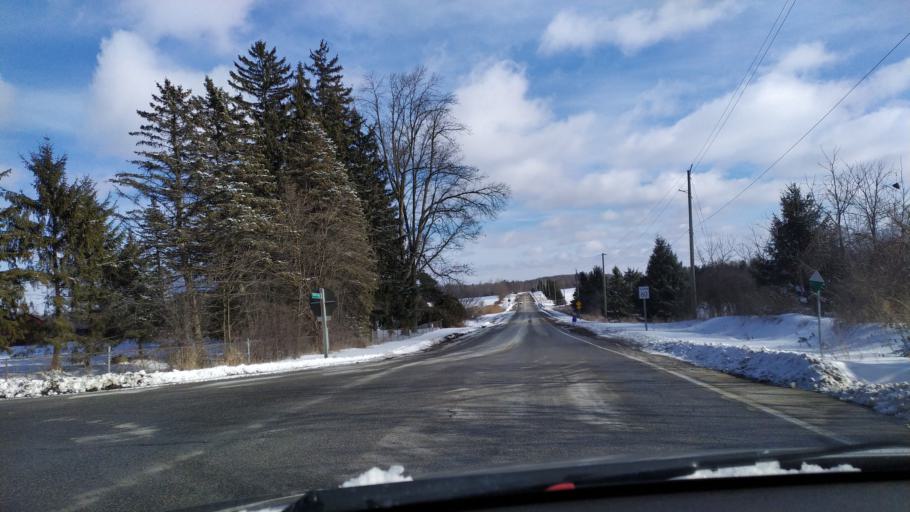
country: CA
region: Ontario
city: Waterloo
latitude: 43.4750
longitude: -80.6910
